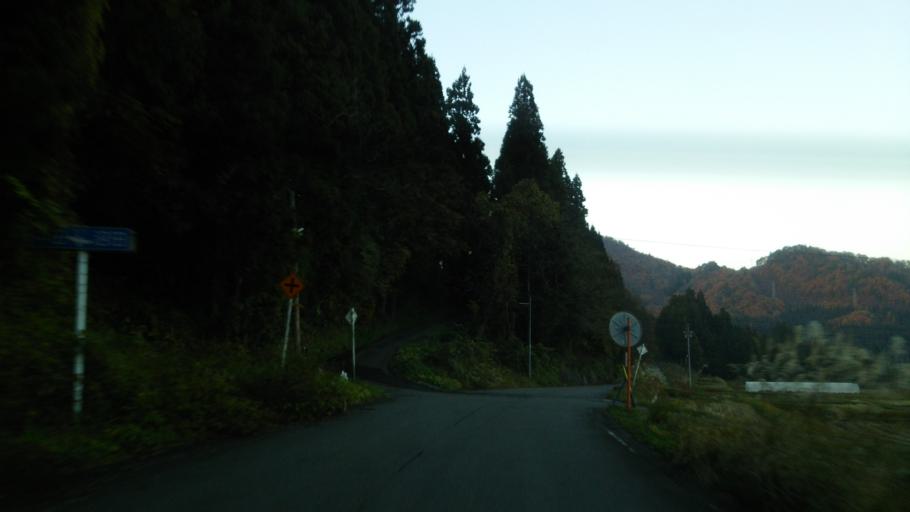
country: JP
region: Fukushima
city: Kitakata
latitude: 37.4875
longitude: 139.6632
